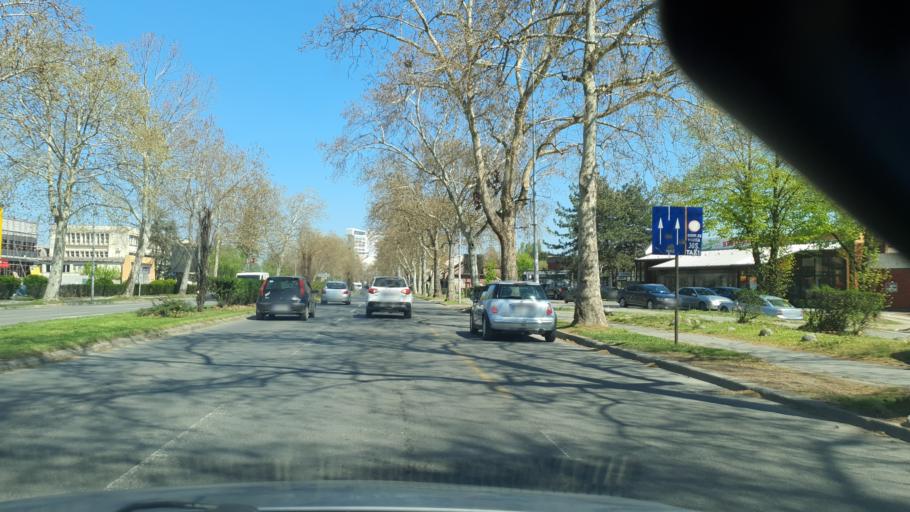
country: RS
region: Autonomna Pokrajina Vojvodina
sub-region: Juznobacki Okrug
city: Novi Sad
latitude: 45.2475
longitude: 19.8085
